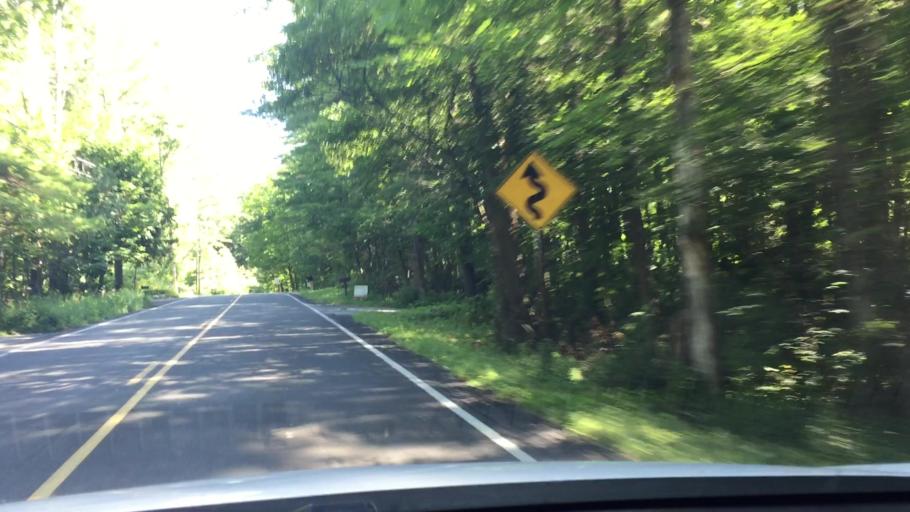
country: US
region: Massachusetts
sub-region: Berkshire County
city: West Stockbridge
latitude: 42.3044
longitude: -73.3726
